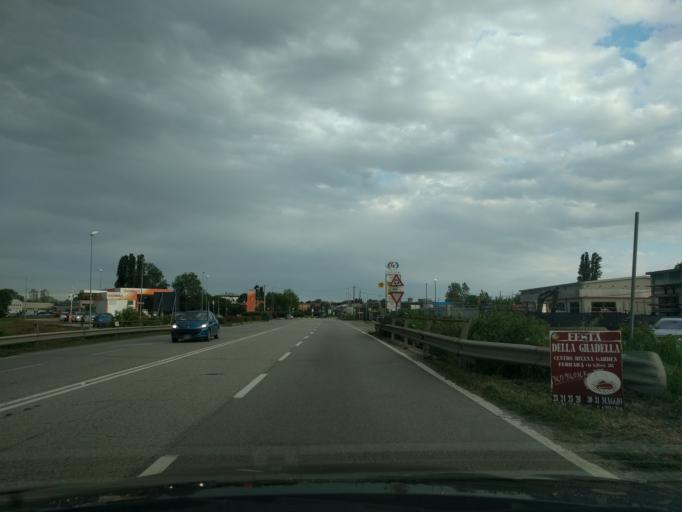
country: IT
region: Emilia-Romagna
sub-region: Provincia di Ferrara
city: Ferrara
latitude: 44.8528
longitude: 11.5862
